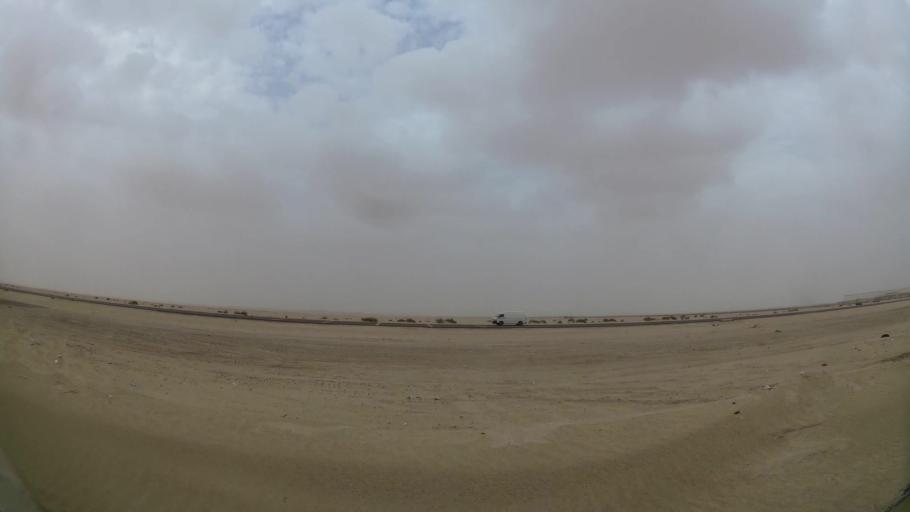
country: AE
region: Abu Dhabi
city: Abu Dhabi
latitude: 24.4490
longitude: 54.7100
